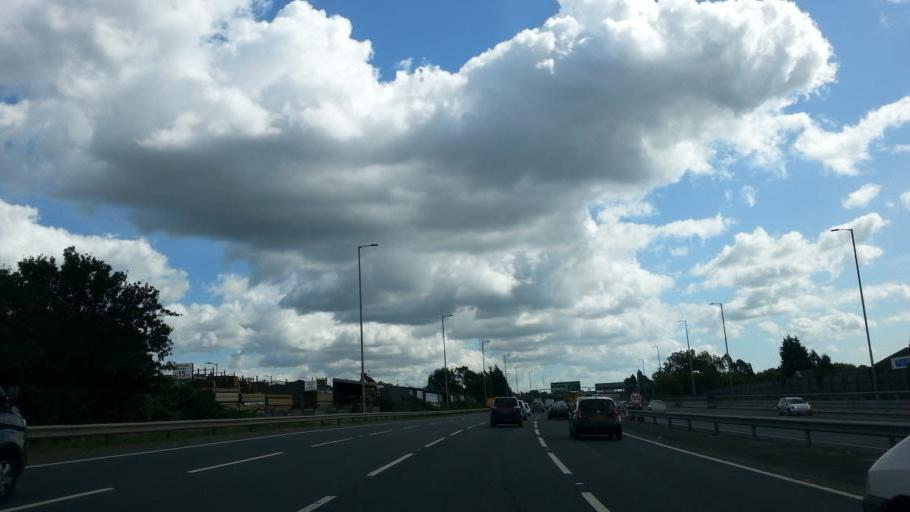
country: GB
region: England
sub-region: Essex
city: Pitsea
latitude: 51.5649
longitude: 0.5112
